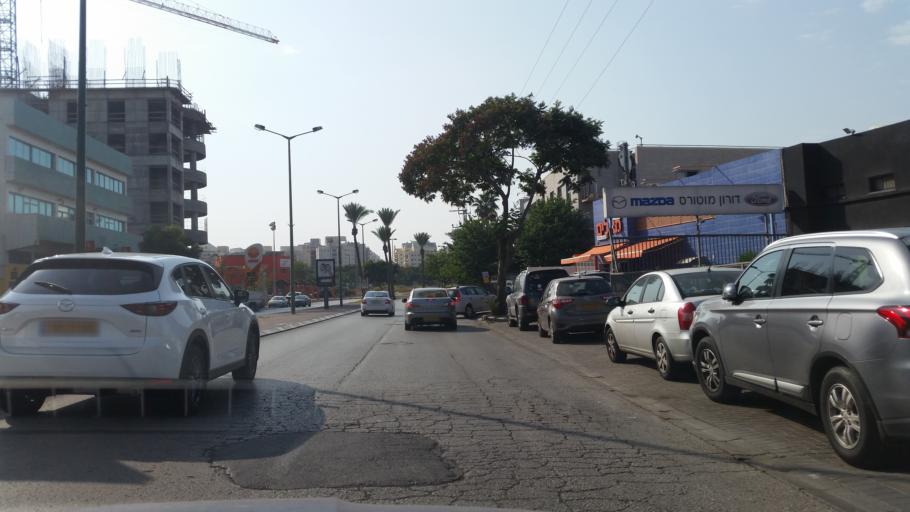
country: IL
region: Central District
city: Bet Yizhaq
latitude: 32.3147
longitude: 34.8736
